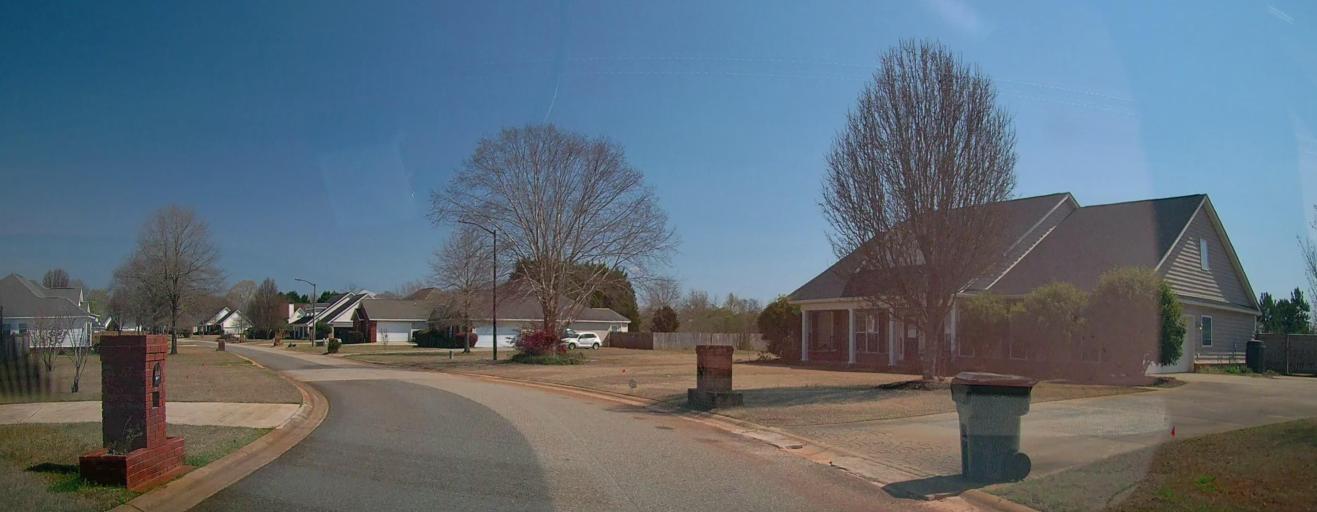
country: US
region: Georgia
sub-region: Houston County
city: Centerville
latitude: 32.5813
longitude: -83.7134
